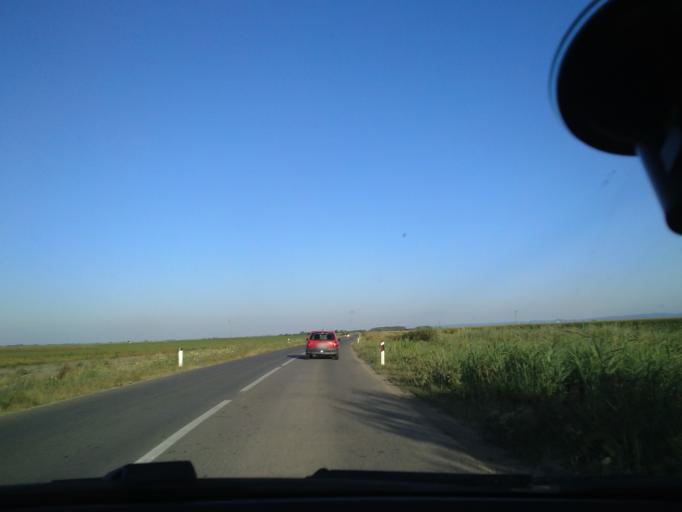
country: RS
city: Maglic
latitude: 45.3847
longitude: 19.5060
